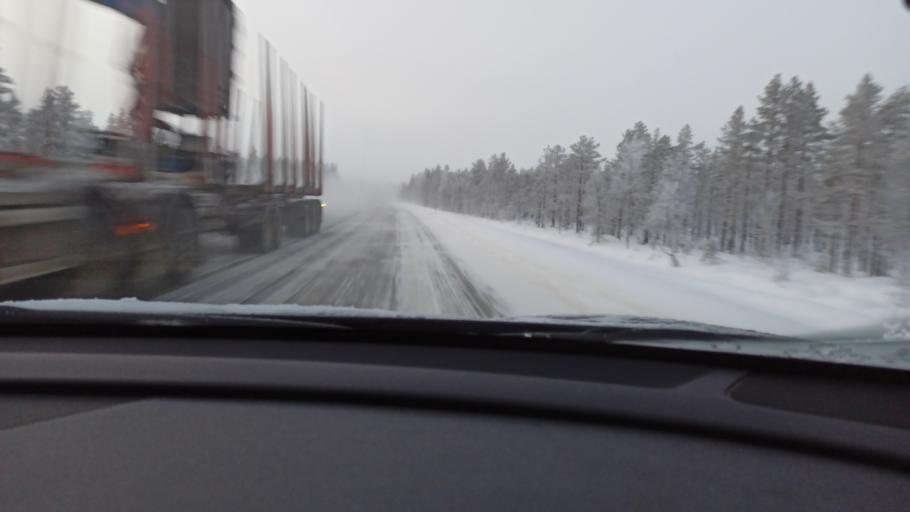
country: FI
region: Lapland
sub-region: Pohjois-Lappi
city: Sodankylae
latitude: 66.9747
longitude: 26.3123
